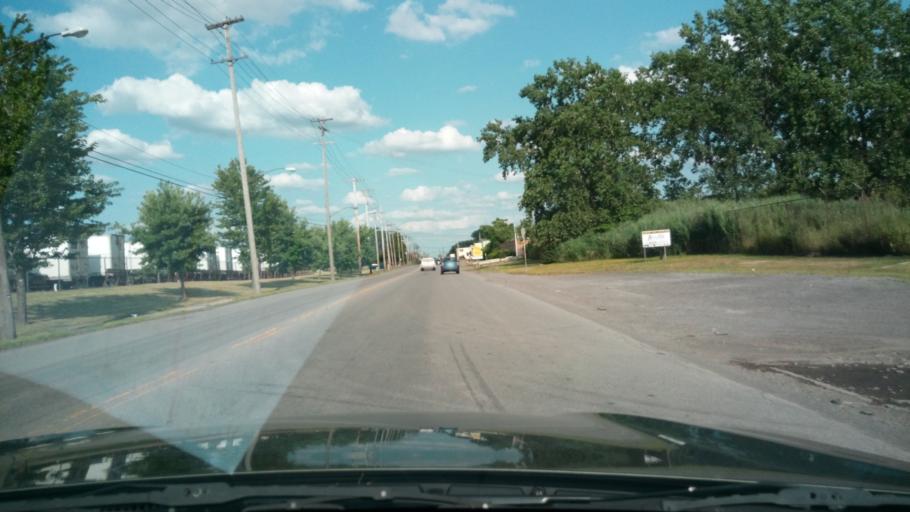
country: US
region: New York
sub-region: Erie County
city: Sloan
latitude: 42.8848
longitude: -78.8232
